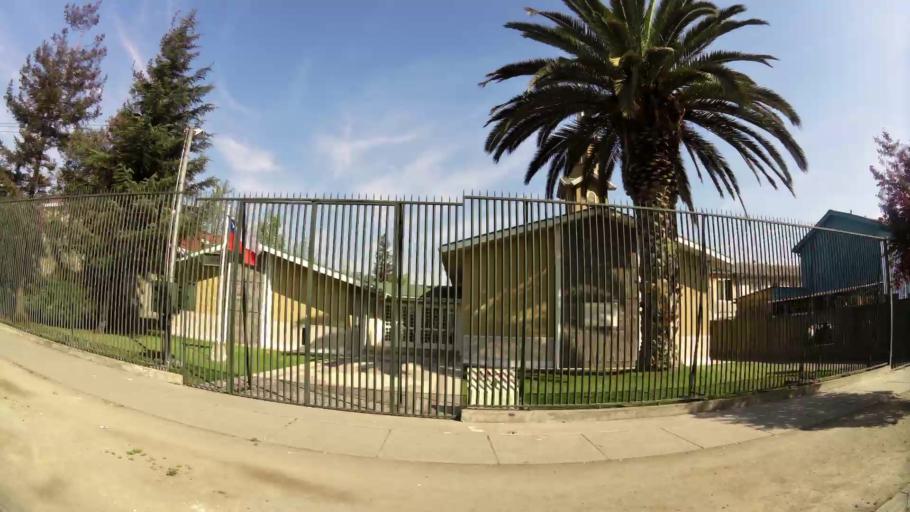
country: CL
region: Santiago Metropolitan
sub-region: Provincia de Santiago
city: La Pintana
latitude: -33.5574
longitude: -70.6666
